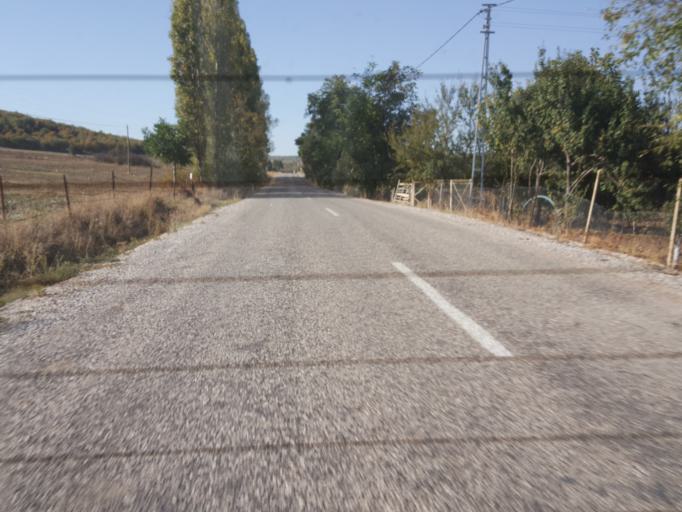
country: TR
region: Corum
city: Seydim
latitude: 40.5538
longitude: 34.7562
